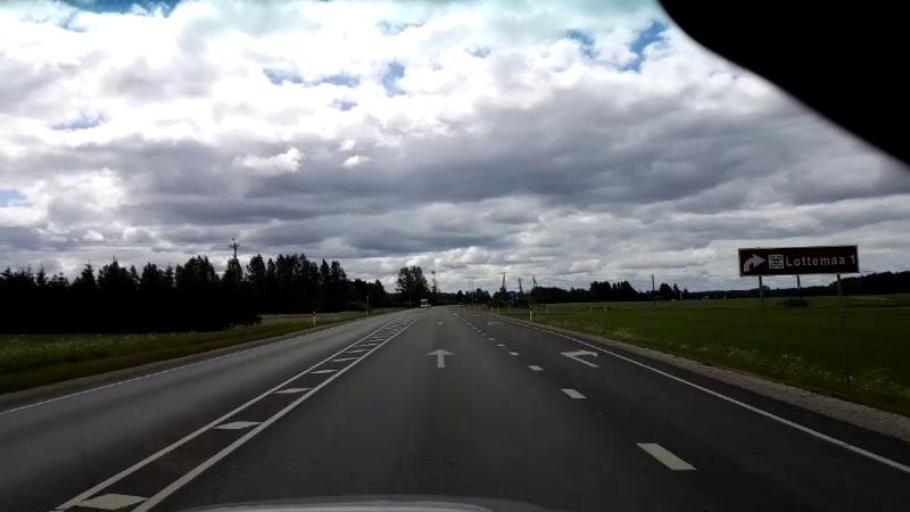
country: EE
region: Paernumaa
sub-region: Paikuse vald
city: Paikuse
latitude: 58.3059
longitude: 24.6093
